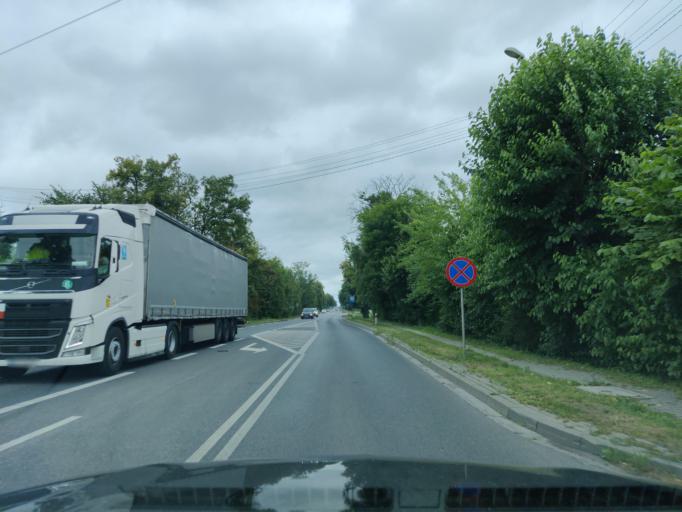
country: PL
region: Masovian Voivodeship
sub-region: Powiat pultuski
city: Pultusk
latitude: 52.6900
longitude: 21.0805
